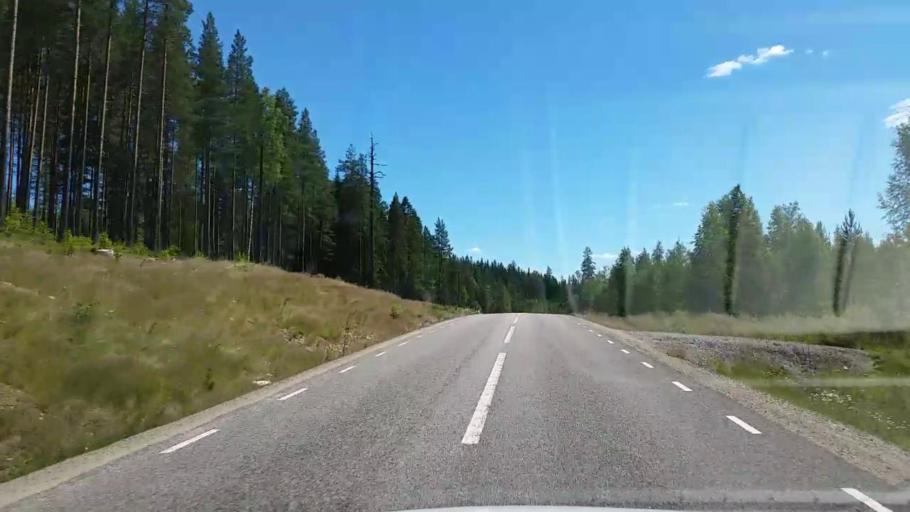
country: SE
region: Gaevleborg
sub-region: Ovanakers Kommun
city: Edsbyn
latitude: 61.5127
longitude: 15.6799
